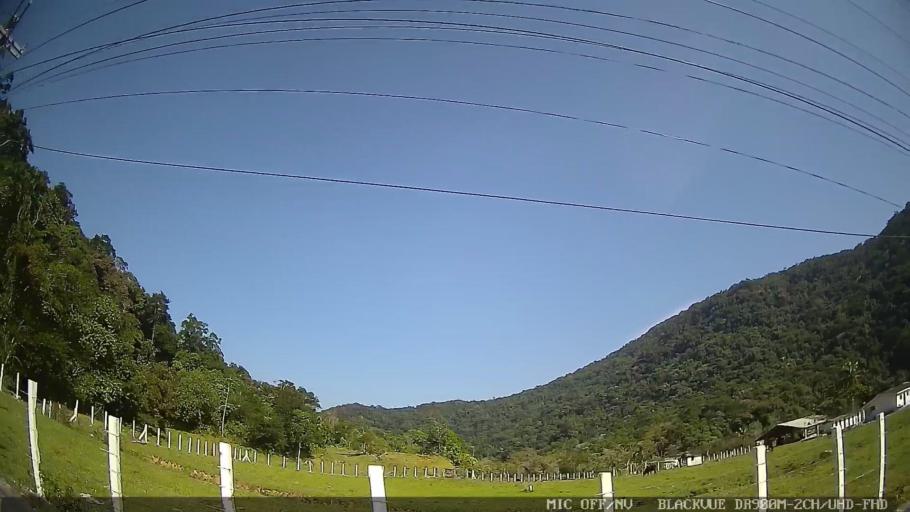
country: BR
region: Sao Paulo
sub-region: Guaruja
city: Guaruja
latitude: -24.0125
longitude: -46.3026
